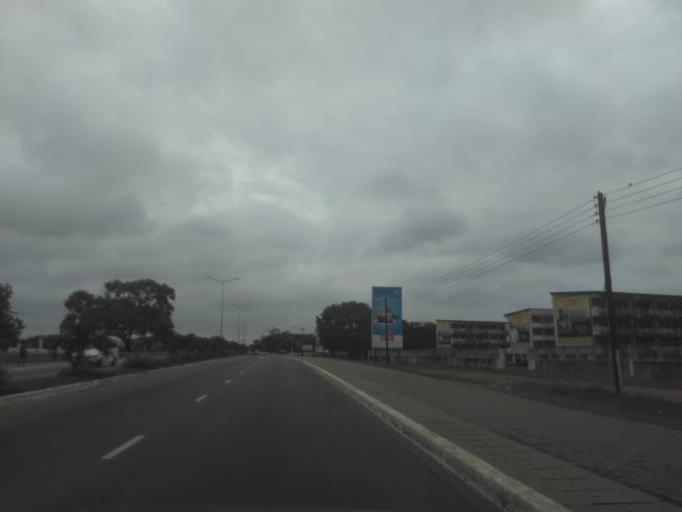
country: GH
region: Greater Accra
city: Accra
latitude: 5.5767
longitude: -0.1877
